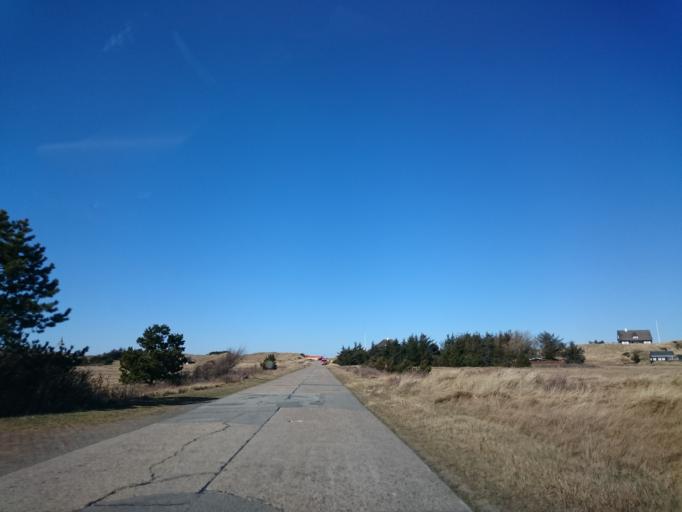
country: DK
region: North Denmark
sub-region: Frederikshavn Kommune
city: Skagen
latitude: 57.7224
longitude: 10.5300
